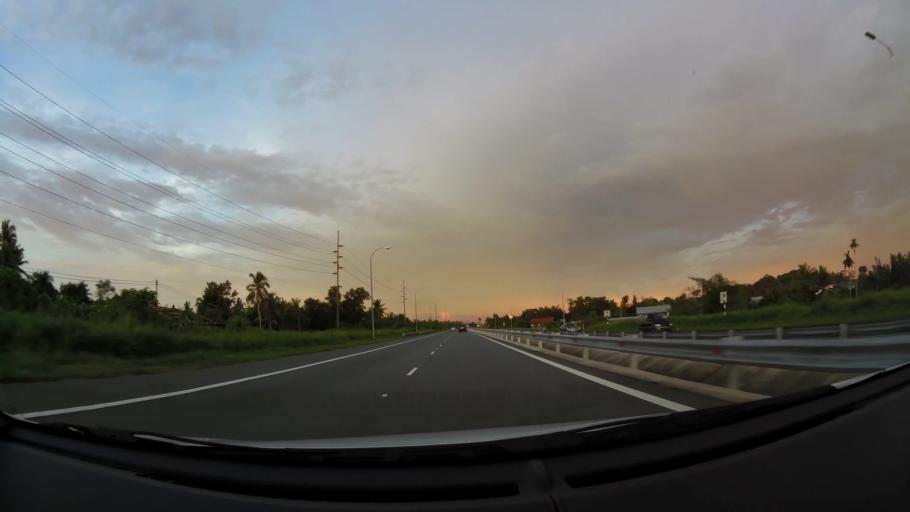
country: BN
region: Belait
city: Kuala Belait
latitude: 4.5805
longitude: 114.2461
